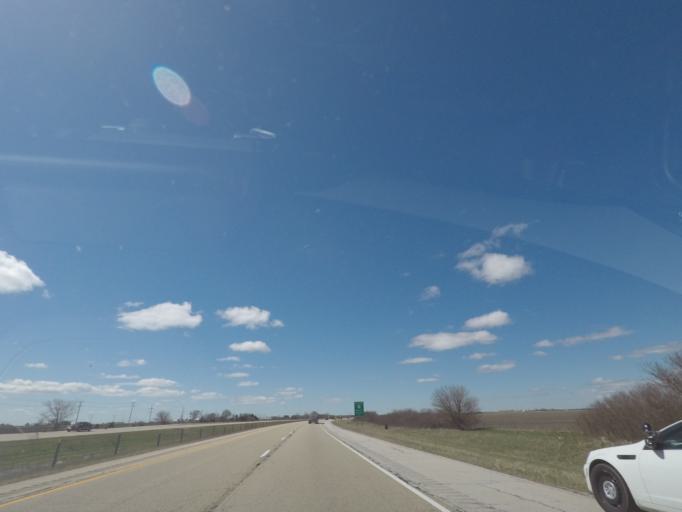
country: US
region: Illinois
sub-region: Livingston County
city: Dwight
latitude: 41.1246
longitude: -88.3892
